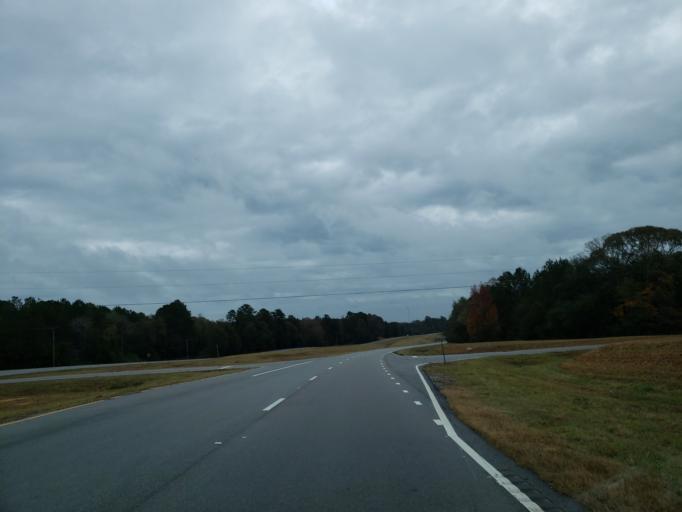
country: US
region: Mississippi
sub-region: Wayne County
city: Waynesboro
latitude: 31.6959
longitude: -88.7239
